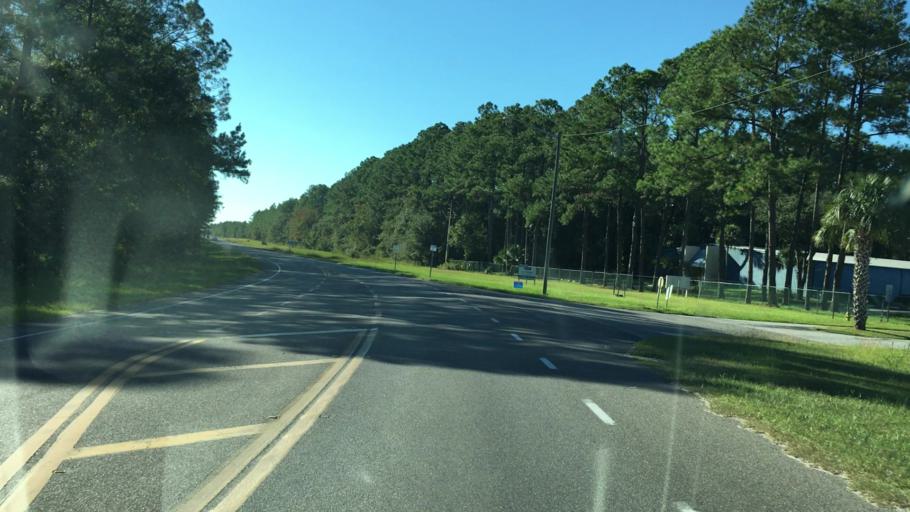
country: US
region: Florida
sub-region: Alachua County
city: Gainesville
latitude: 29.7029
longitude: -82.2785
